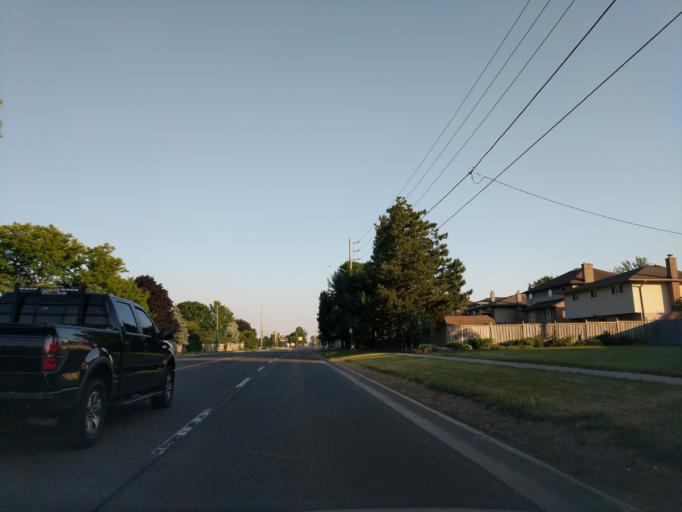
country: CA
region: Ontario
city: Oshawa
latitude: 43.9106
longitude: -78.9016
